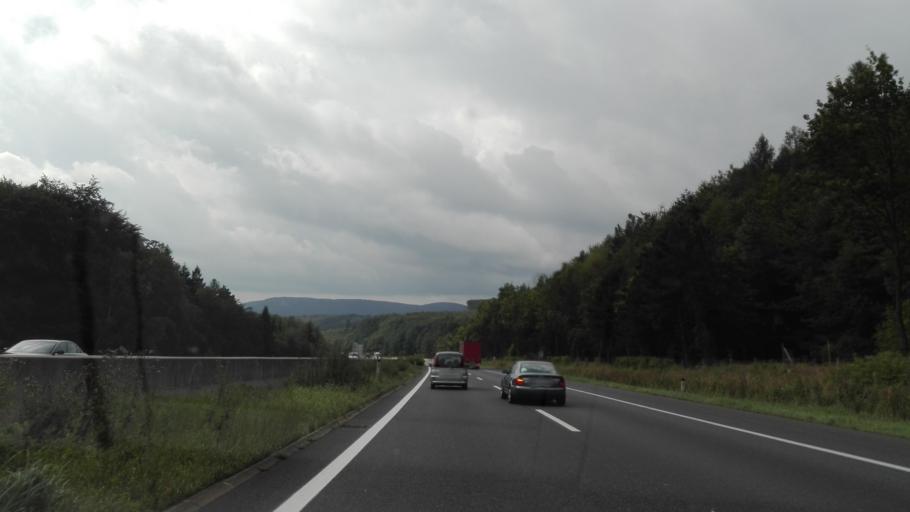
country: AT
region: Lower Austria
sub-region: Politischer Bezirk Sankt Polten
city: Eichgraben
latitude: 48.1230
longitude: 15.9704
